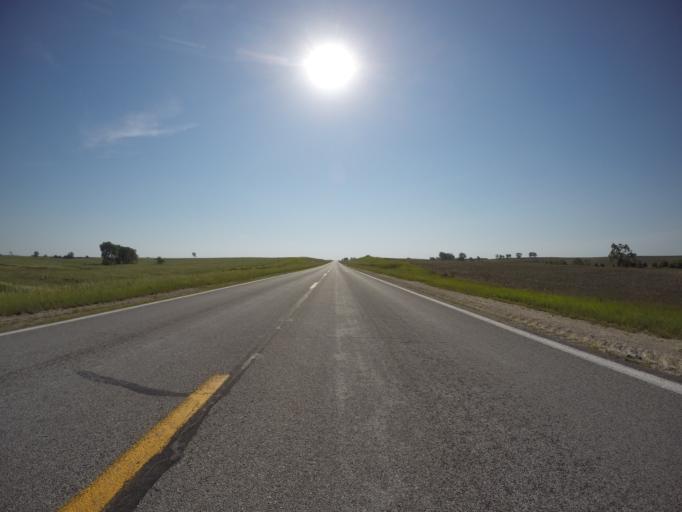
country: US
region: Nebraska
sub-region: Pawnee County
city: Pawnee City
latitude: 40.0447
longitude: -96.3669
